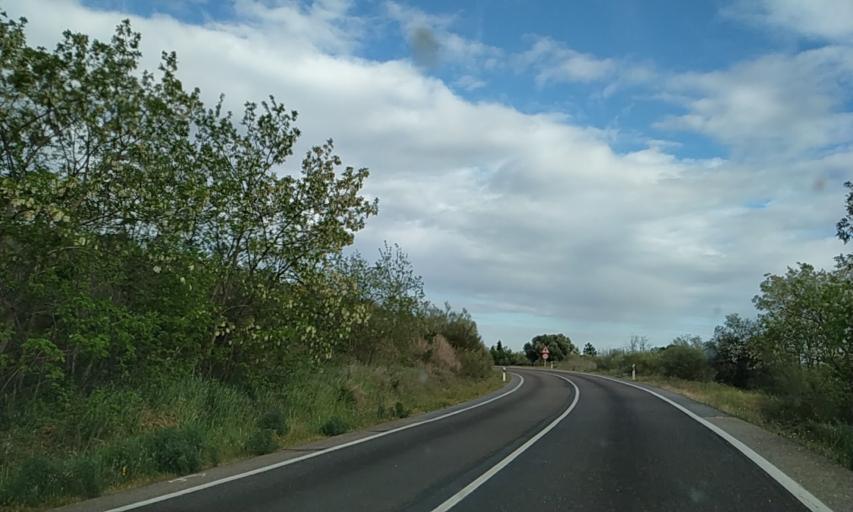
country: ES
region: Extremadura
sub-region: Provincia de Caceres
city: Coria
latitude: 40.0070
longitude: -6.5584
